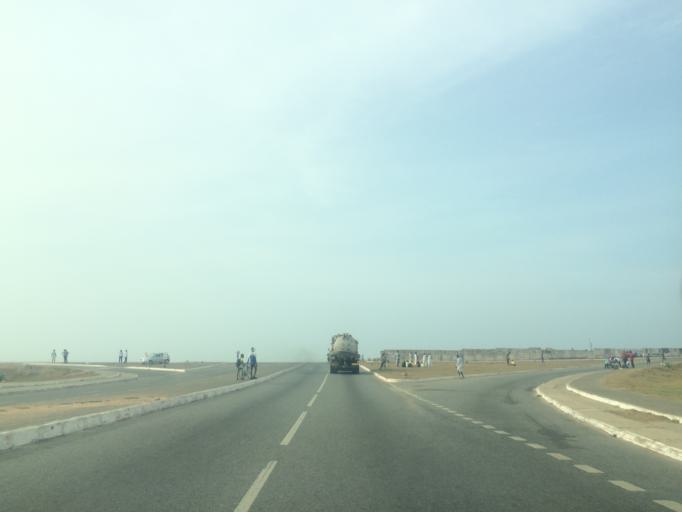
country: GH
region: Greater Accra
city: Accra
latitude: 5.5316
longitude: -0.2220
